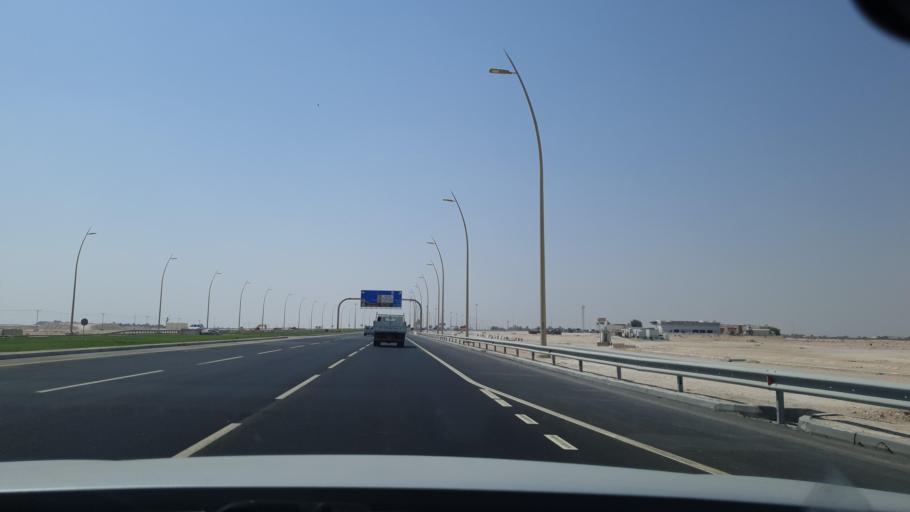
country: QA
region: Al Khawr
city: Al Khawr
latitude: 25.6557
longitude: 51.4607
